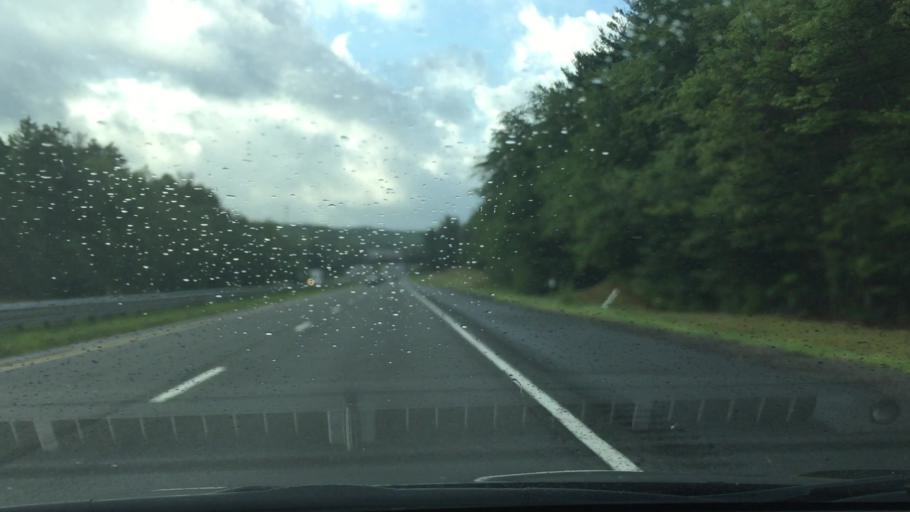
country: US
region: Massachusetts
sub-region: Hampden County
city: Palmer
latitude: 42.1731
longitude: -72.3040
